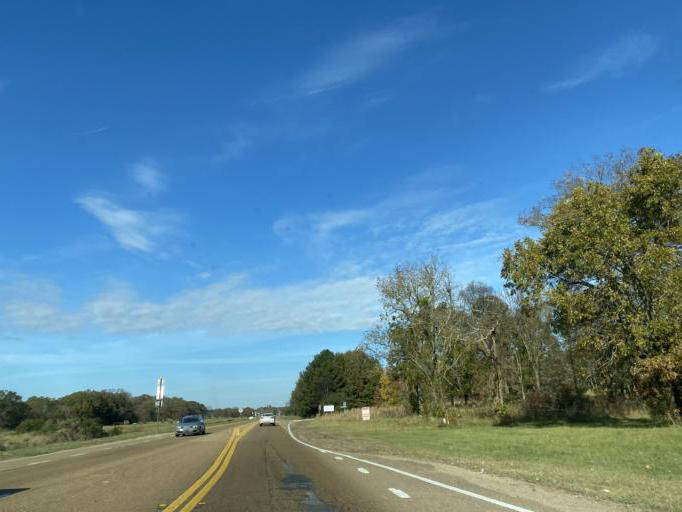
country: US
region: Mississippi
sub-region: Madison County
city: Madison
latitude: 32.4744
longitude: -90.1504
